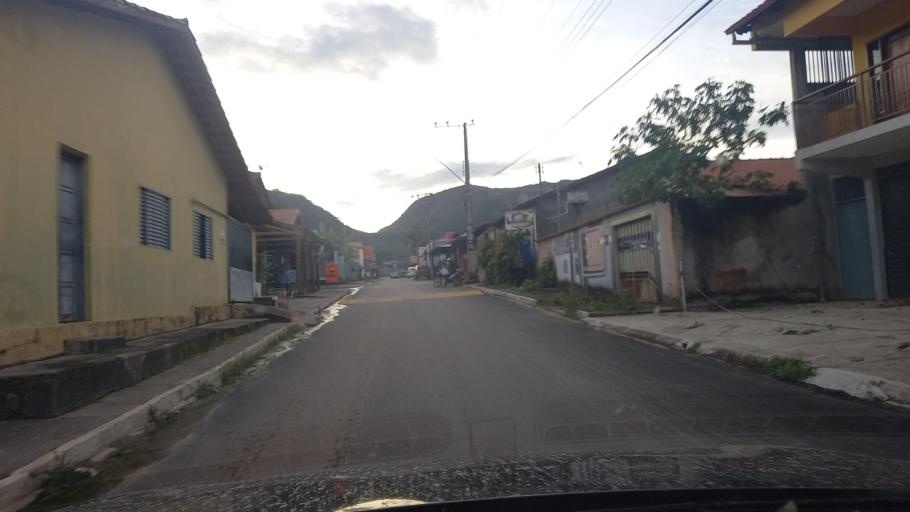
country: BR
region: Goias
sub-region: Cavalcante
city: Cavalcante
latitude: -13.7972
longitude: -47.4583
